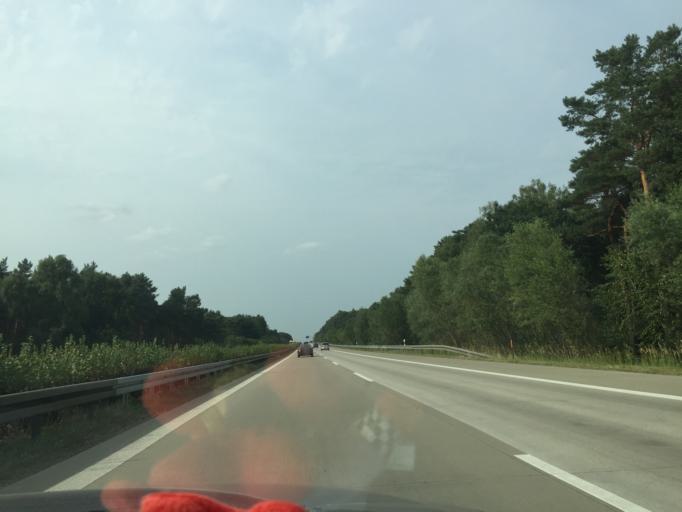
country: DE
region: Brandenburg
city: Bestensee
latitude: 52.2312
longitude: 13.5940
